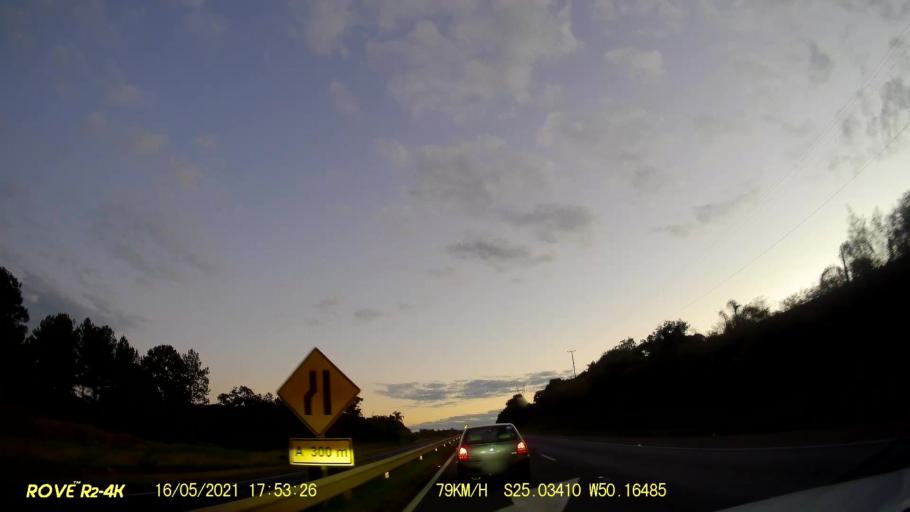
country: BR
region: Parana
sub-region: Ponta Grossa
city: Ponta Grossa
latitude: -25.0345
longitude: -50.1653
